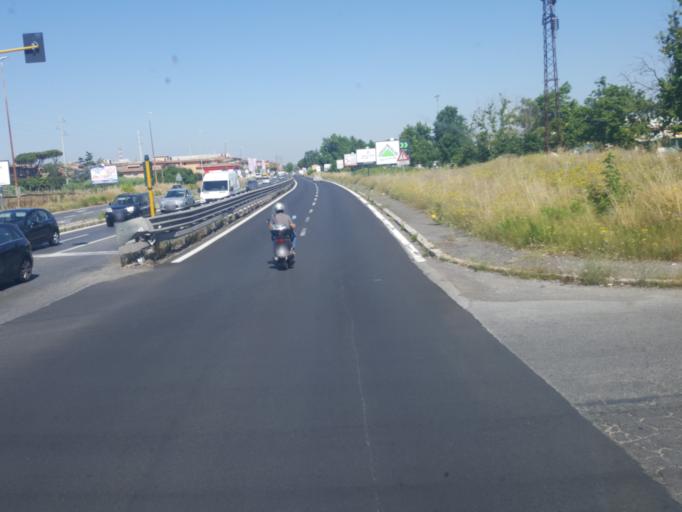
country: IT
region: Latium
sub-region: Citta metropolitana di Roma Capitale
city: Ciampino
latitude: 41.8344
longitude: 12.6067
